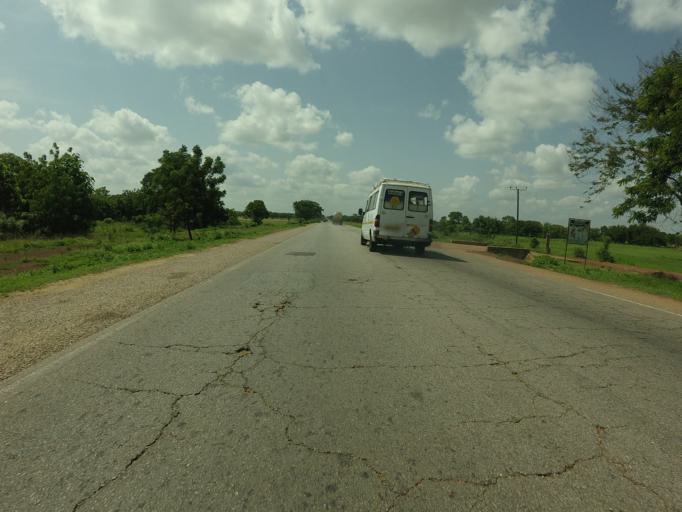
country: GH
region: Northern
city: Savelugu
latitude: 9.5641
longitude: -0.8360
